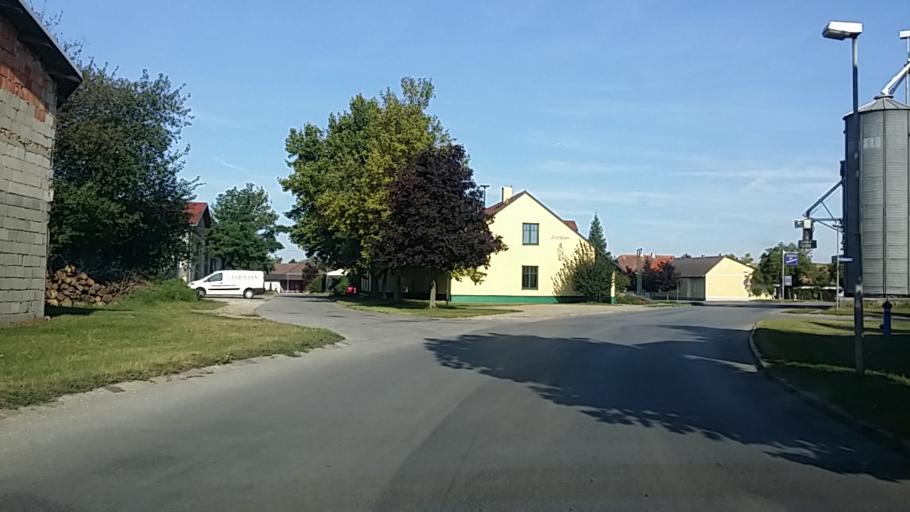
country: AT
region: Burgenland
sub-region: Politischer Bezirk Neusiedl am See
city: Pamhagen
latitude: 47.7001
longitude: 16.9082
